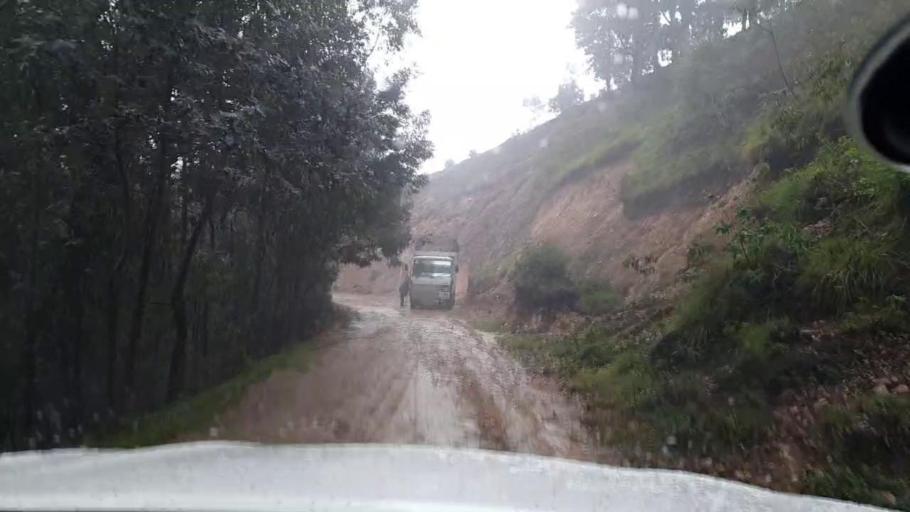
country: RW
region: Western Province
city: Kibuye
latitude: -2.1347
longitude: 29.4620
